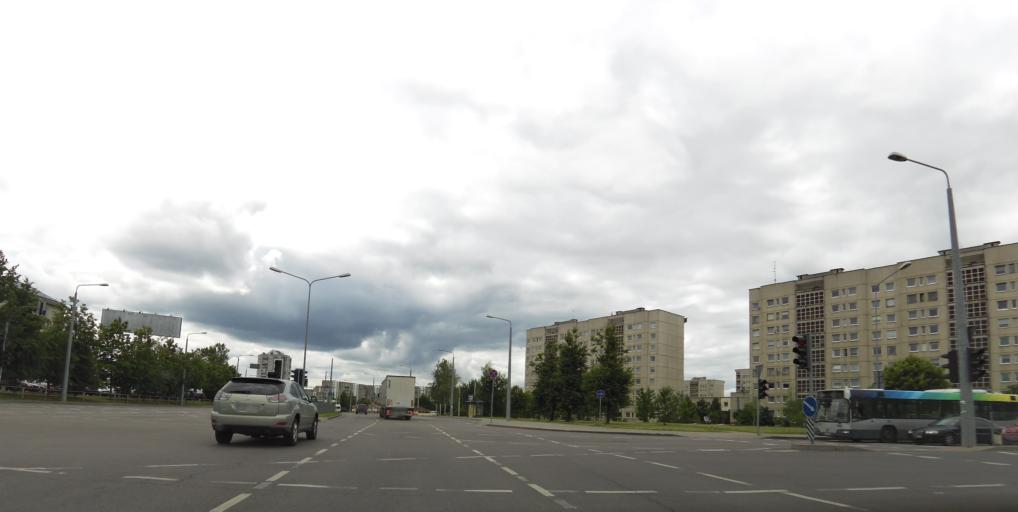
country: LT
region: Vilnius County
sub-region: Vilnius
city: Fabijoniskes
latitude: 54.7296
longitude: 25.2367
